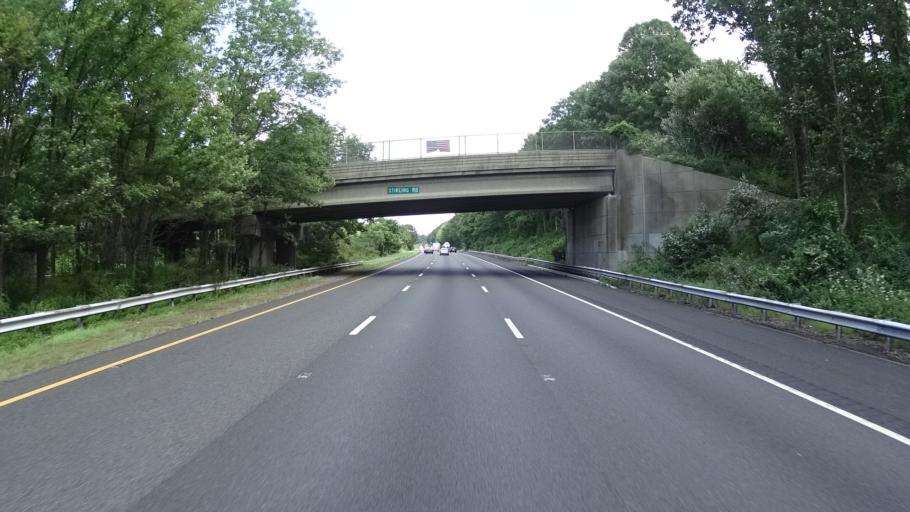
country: US
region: New Jersey
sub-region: Somerset County
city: Watchung
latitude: 40.6491
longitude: -74.4786
